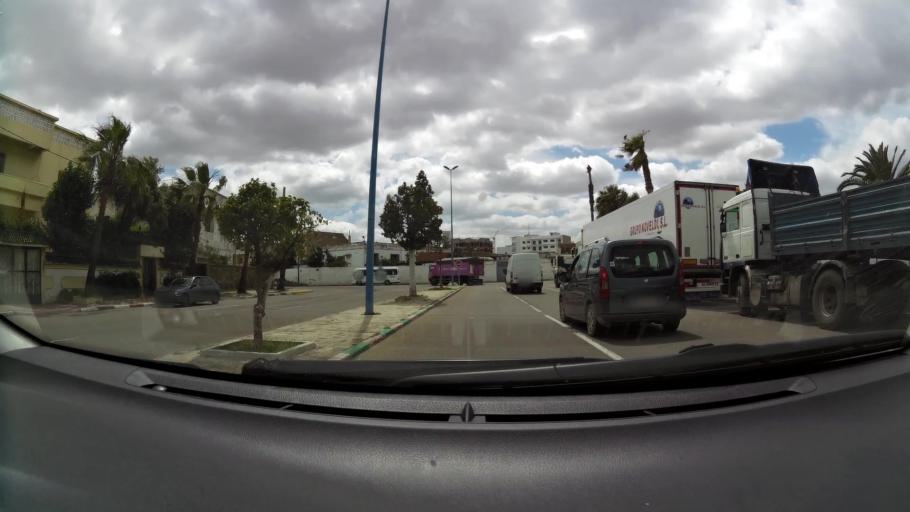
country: MA
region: Grand Casablanca
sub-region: Casablanca
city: Casablanca
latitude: 33.6082
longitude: -7.5481
